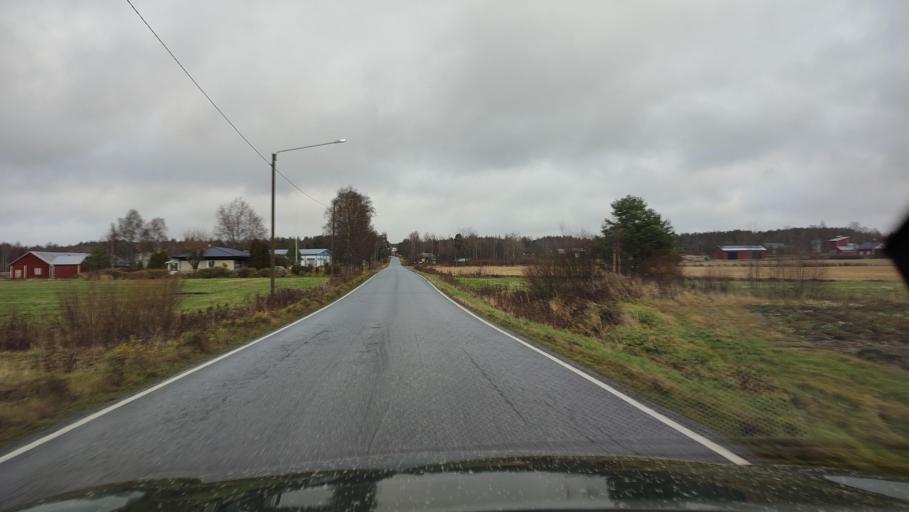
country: FI
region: Ostrobothnia
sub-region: Sydosterbotten
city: Kristinestad
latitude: 62.3106
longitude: 21.4820
